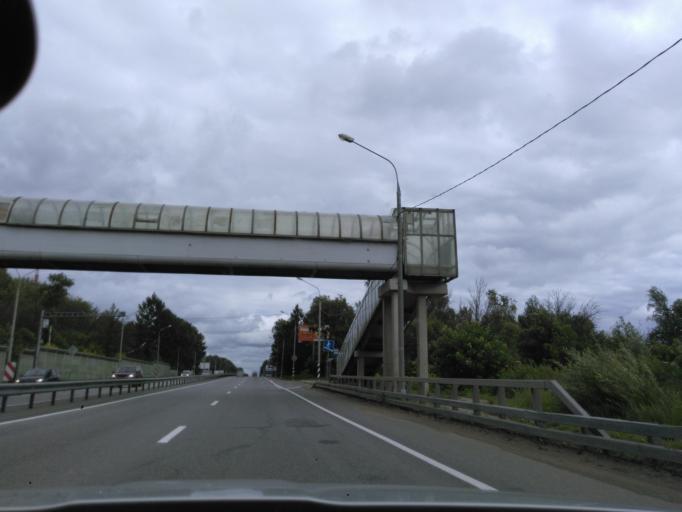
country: RU
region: Moskovskaya
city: Chashnikovo
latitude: 56.0276
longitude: 37.1733
